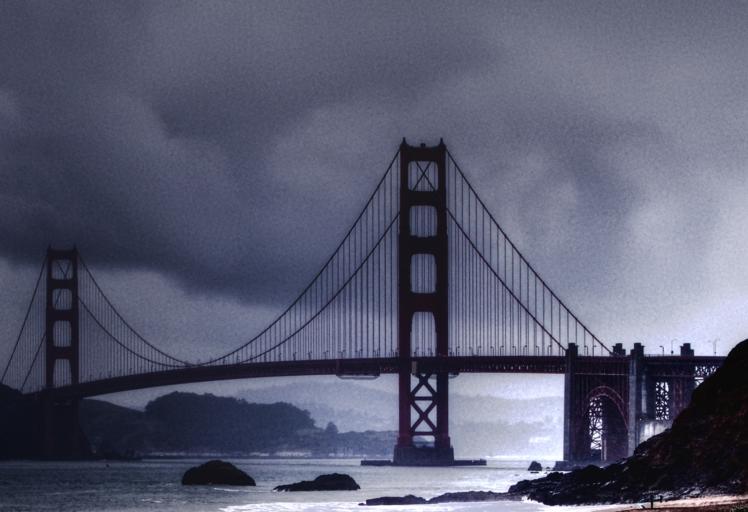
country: US
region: California
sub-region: Marin County
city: Sausalito
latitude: 37.7971
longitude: -122.4794
